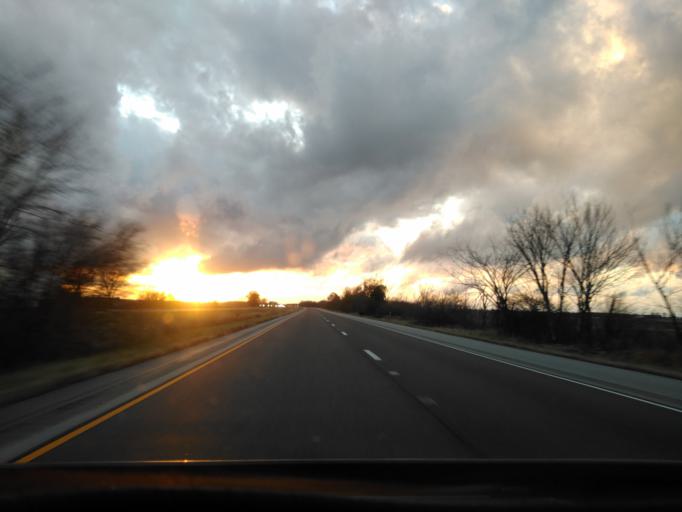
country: US
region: Illinois
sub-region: Fayette County
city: Saint Elmo
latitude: 38.9946
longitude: -88.9173
